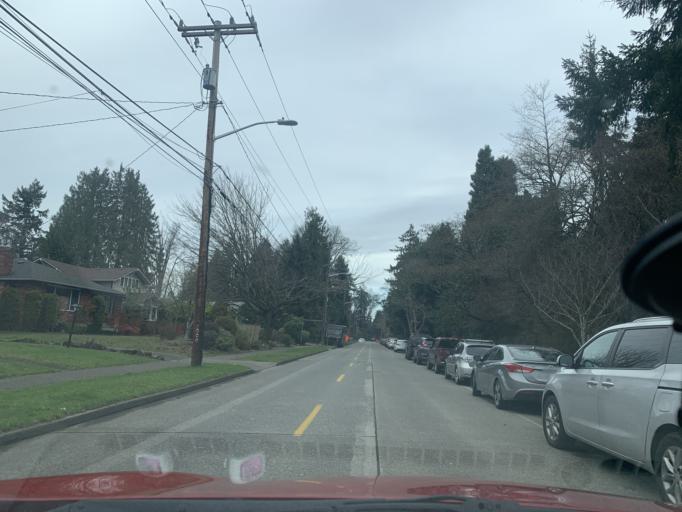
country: US
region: Washington
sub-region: King County
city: Bryn Mawr-Skyway
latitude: 47.5329
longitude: -122.2667
